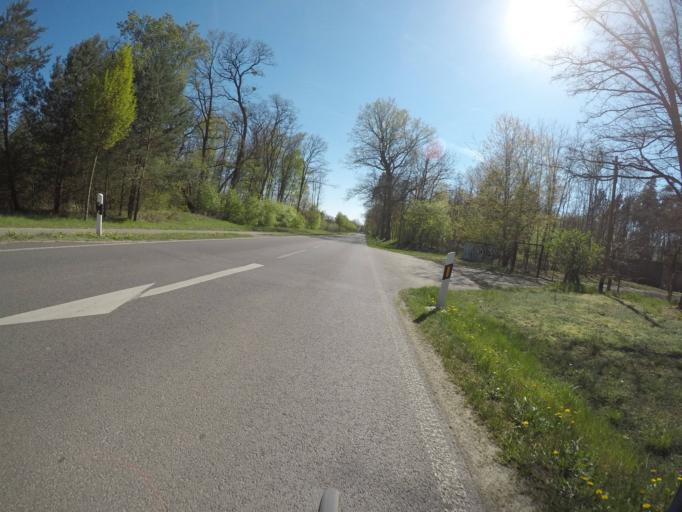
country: DE
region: Brandenburg
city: Rehfelde
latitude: 52.5392
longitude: 13.9357
